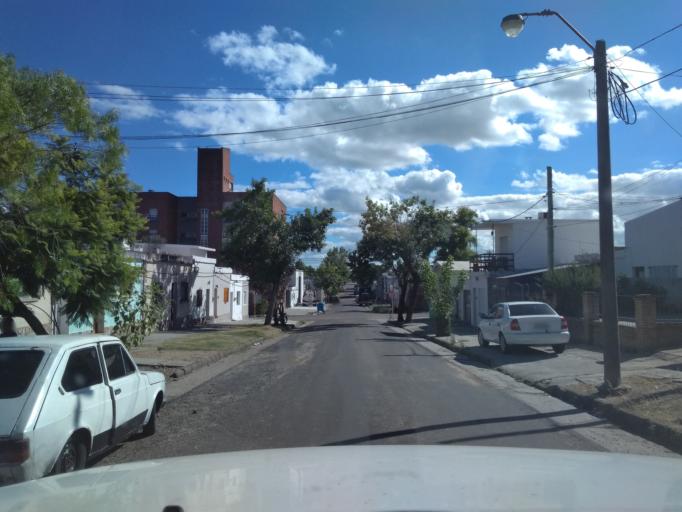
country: UY
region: Florida
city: Florida
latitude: -34.1018
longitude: -56.2090
